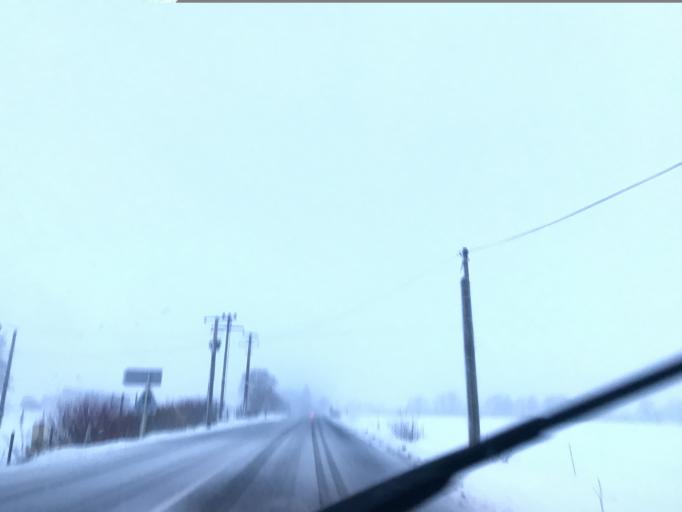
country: FR
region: Auvergne
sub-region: Departement du Puy-de-Dome
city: Saint-Sauves-d'Auvergne
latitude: 45.6491
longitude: 2.7052
